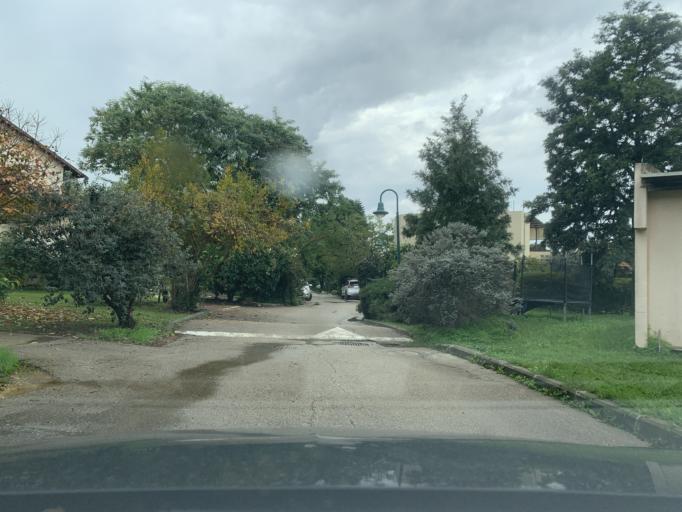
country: PS
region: West Bank
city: Qalqilyah
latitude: 32.2134
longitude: 34.9801
